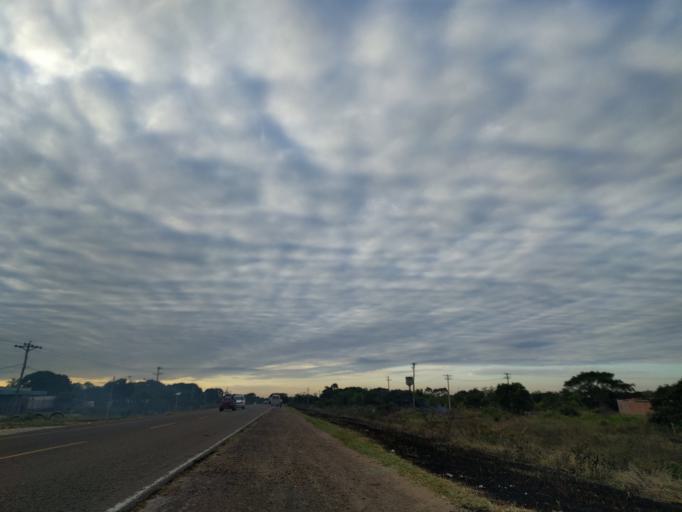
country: BO
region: Santa Cruz
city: Santa Rita
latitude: -17.8831
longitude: -63.2658
